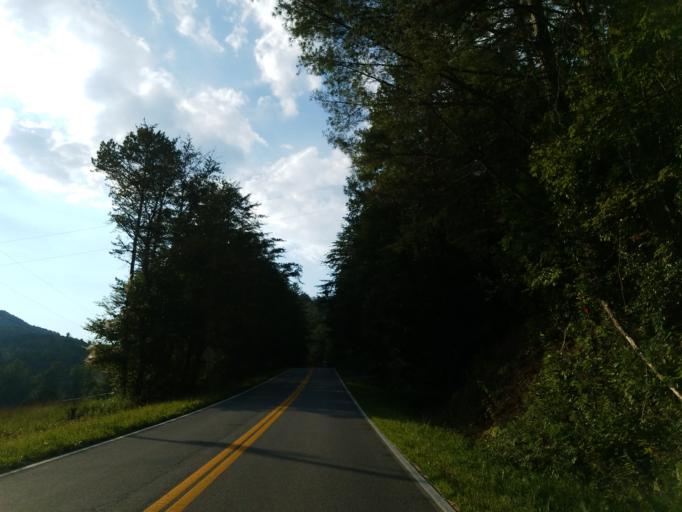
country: US
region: Georgia
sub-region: Fannin County
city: Blue Ridge
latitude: 34.8082
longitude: -84.2842
